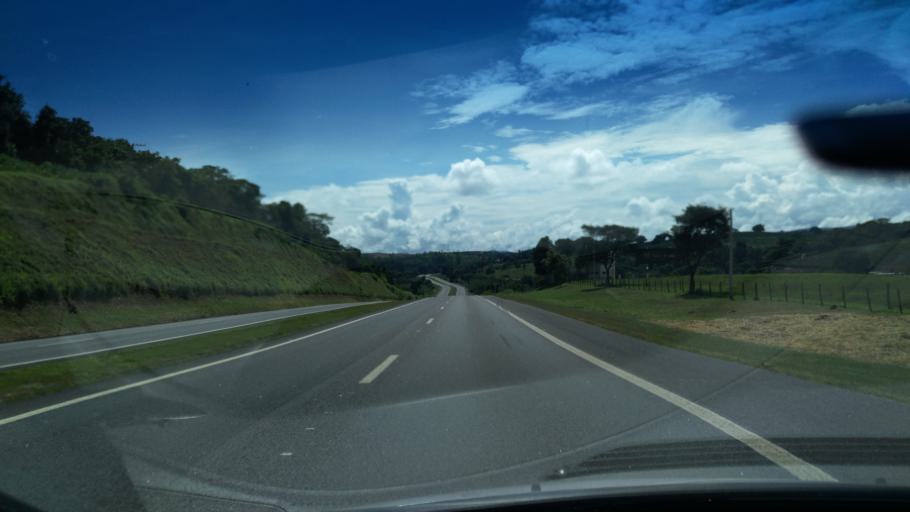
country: BR
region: Sao Paulo
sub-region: Santo Antonio Do Jardim
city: Espirito Santo do Pinhal
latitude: -22.2364
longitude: -46.7987
